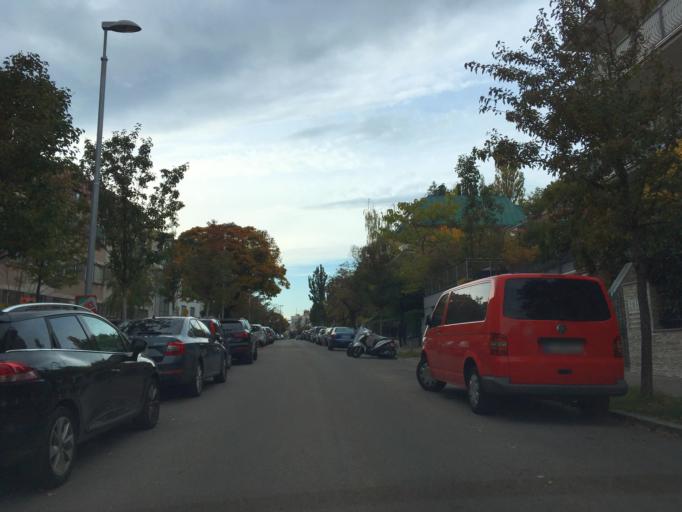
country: AT
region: Vienna
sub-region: Wien Stadt
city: Vienna
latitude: 48.2397
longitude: 16.3221
